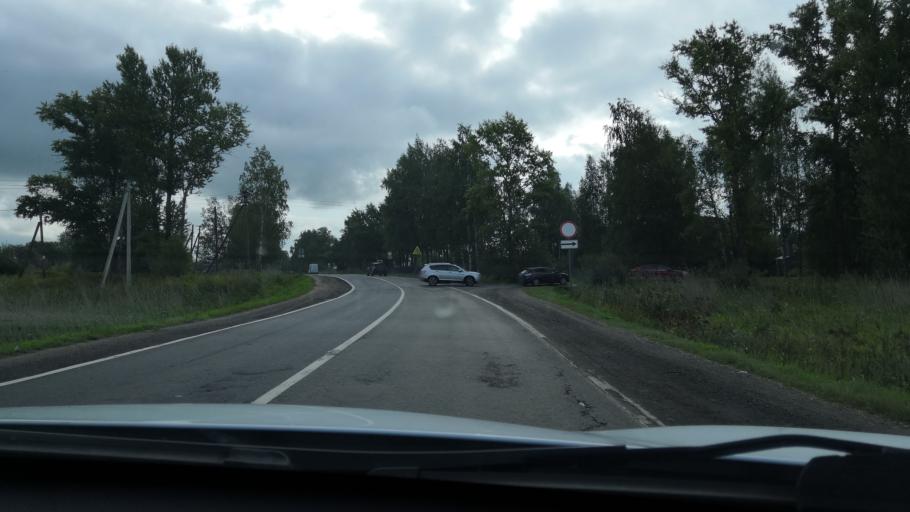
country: RU
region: St.-Petersburg
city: Tyarlevo
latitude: 59.7111
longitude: 30.4692
